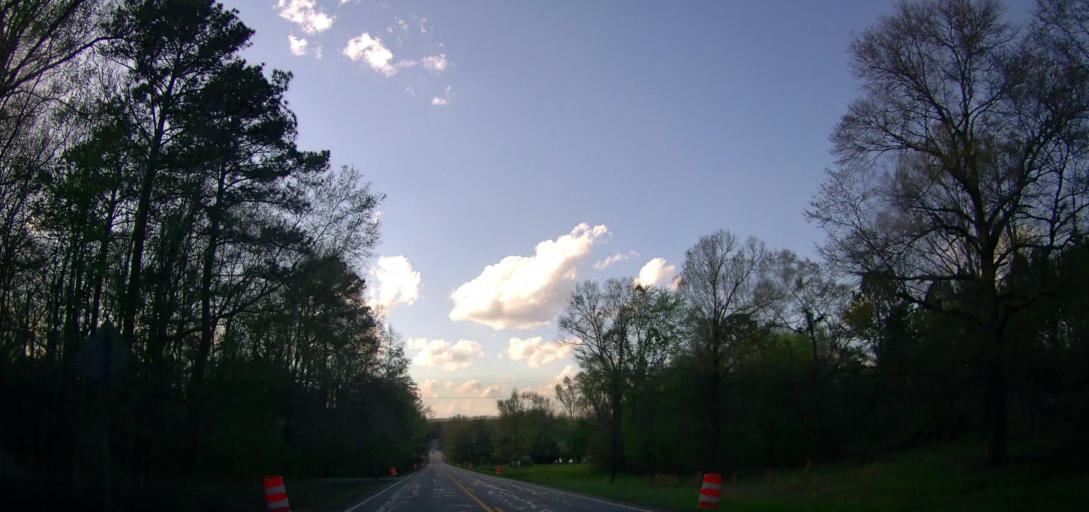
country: US
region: Georgia
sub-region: Putnam County
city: Eatonton
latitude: 33.1784
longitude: -83.4064
